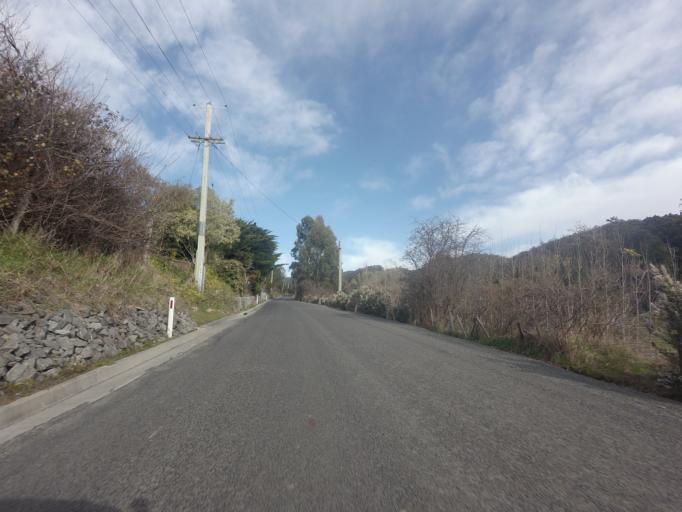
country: AU
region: Tasmania
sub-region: Kingborough
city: Margate
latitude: -42.9895
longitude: 147.1894
